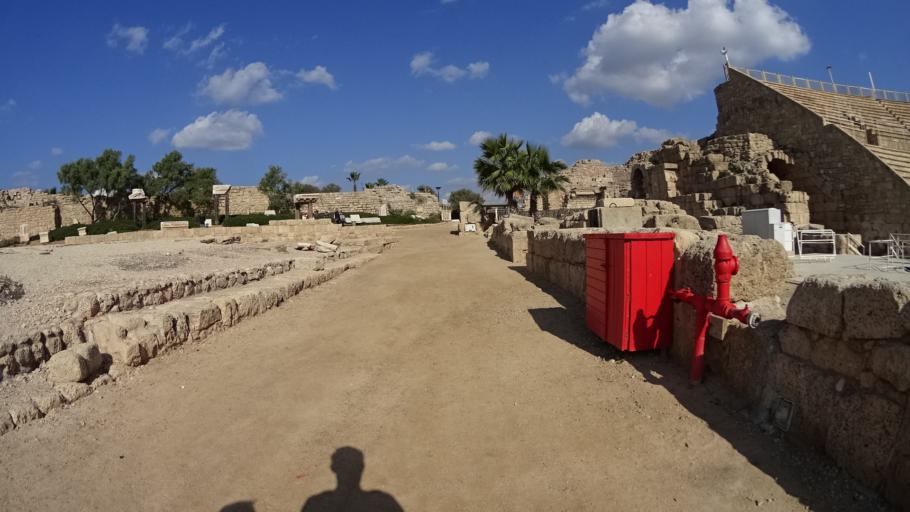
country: IL
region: Haifa
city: Qesarya
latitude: 32.4963
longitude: 34.8909
